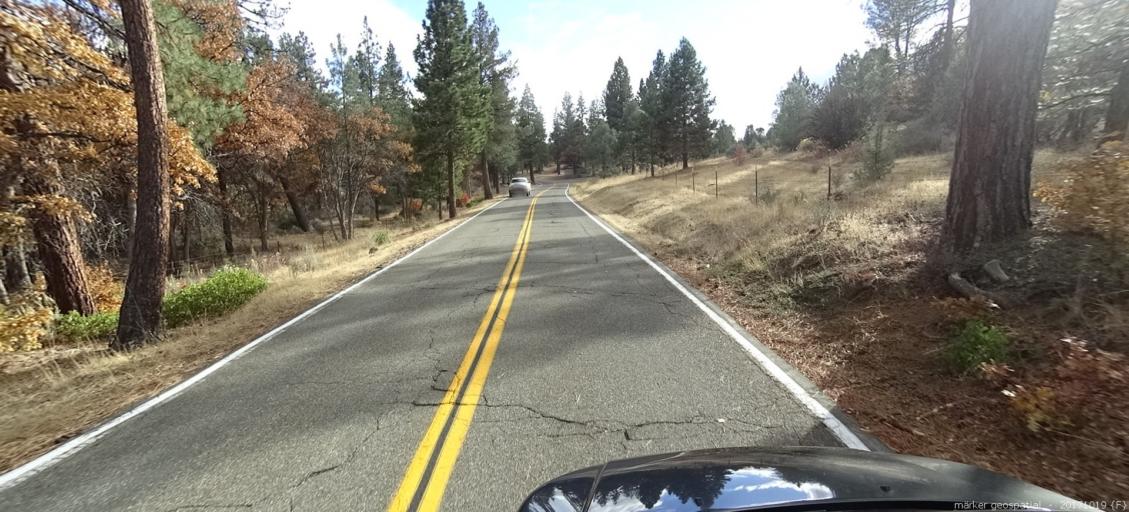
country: US
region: California
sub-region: Shasta County
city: Burney
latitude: 40.9481
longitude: -121.4412
